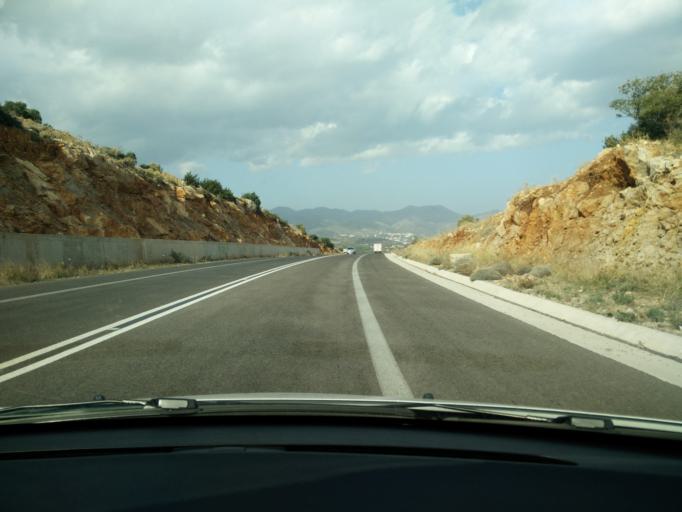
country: GR
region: Crete
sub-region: Nomos Lasithiou
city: Agios Nikolaos
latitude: 35.1736
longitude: 25.7009
